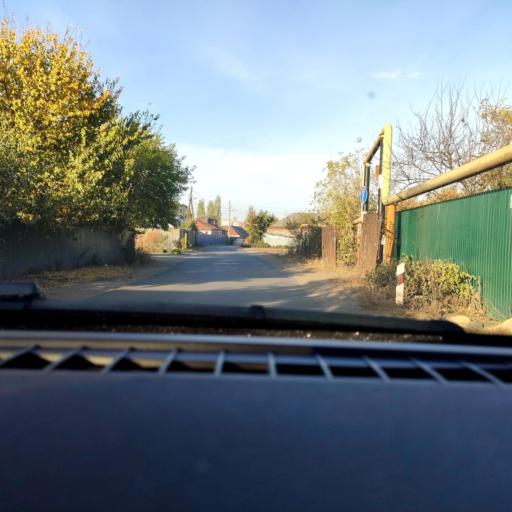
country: RU
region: Voronezj
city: Voronezh
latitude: 51.6680
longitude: 39.2834
